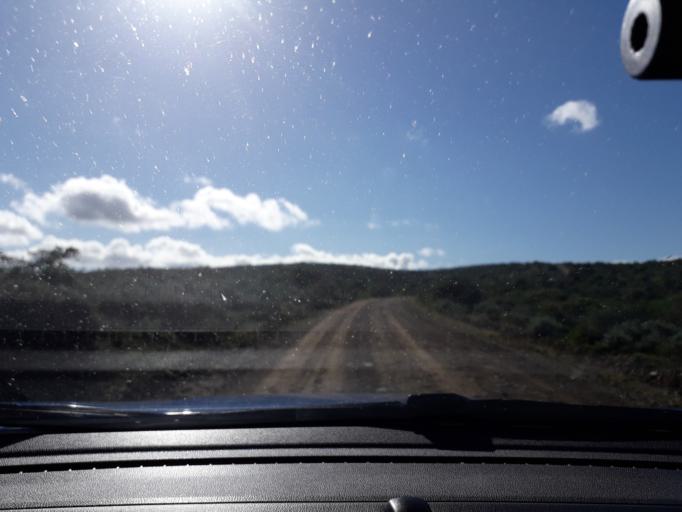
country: ZA
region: Eastern Cape
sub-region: Buffalo City Metropolitan Municipality
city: Bhisho
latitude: -33.1223
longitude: 27.4516
